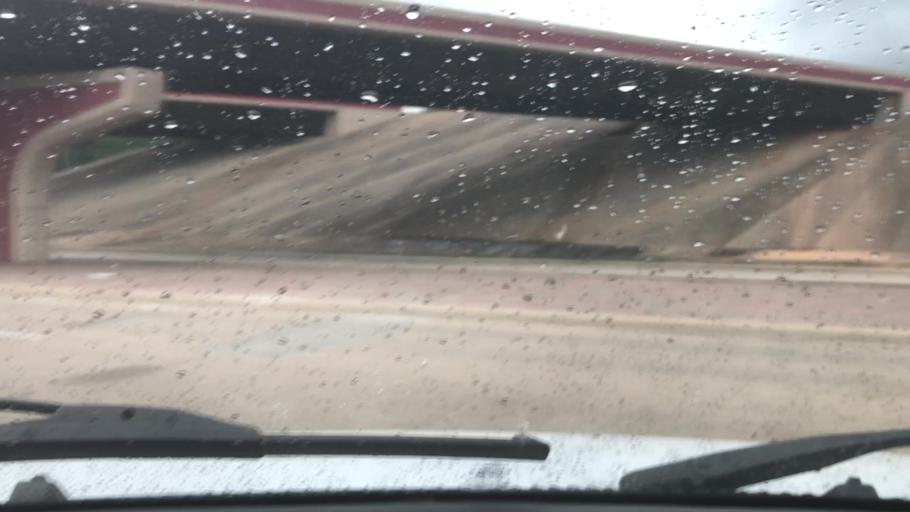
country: US
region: Texas
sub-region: Bowie County
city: Wake Village
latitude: 33.3945
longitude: -94.0986
